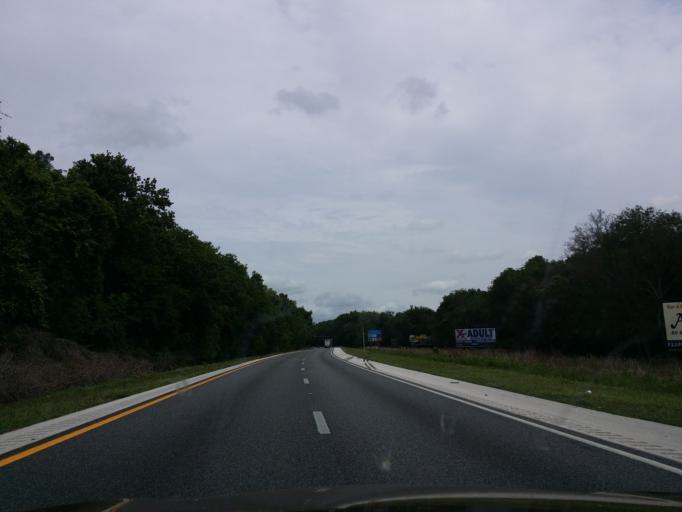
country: US
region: Florida
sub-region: Sumter County
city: Wildwood
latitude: 28.8522
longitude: -82.0907
